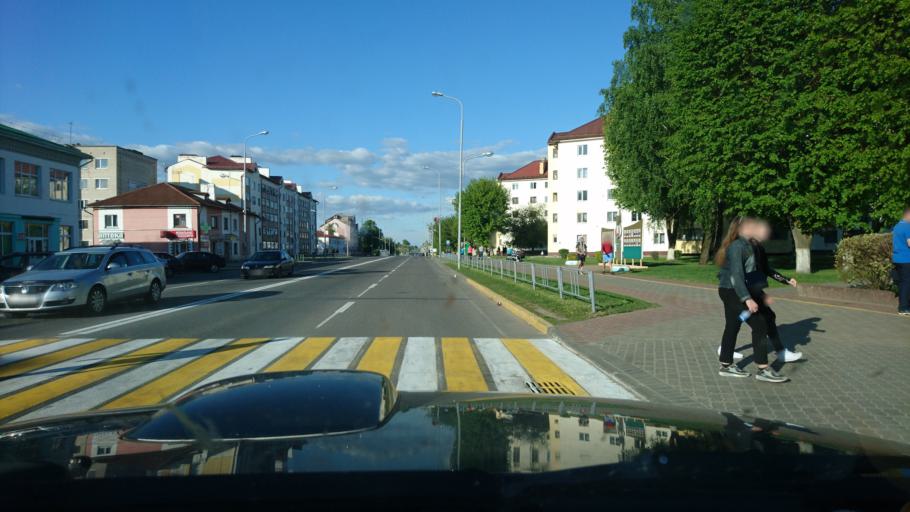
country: BY
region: Brest
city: Ivatsevichy
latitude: 52.7097
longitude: 25.3387
